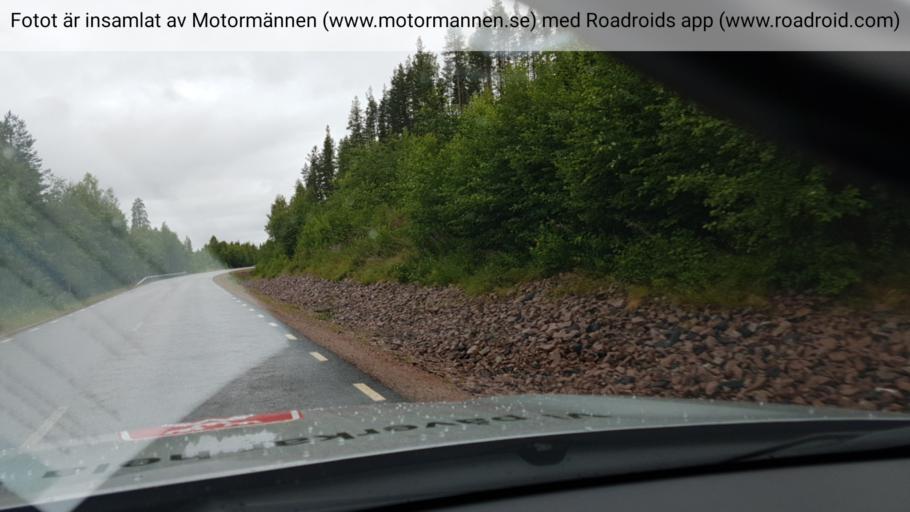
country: SE
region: Norrbotten
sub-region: Gallivare Kommun
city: Gaellivare
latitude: 66.6271
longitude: 20.4159
